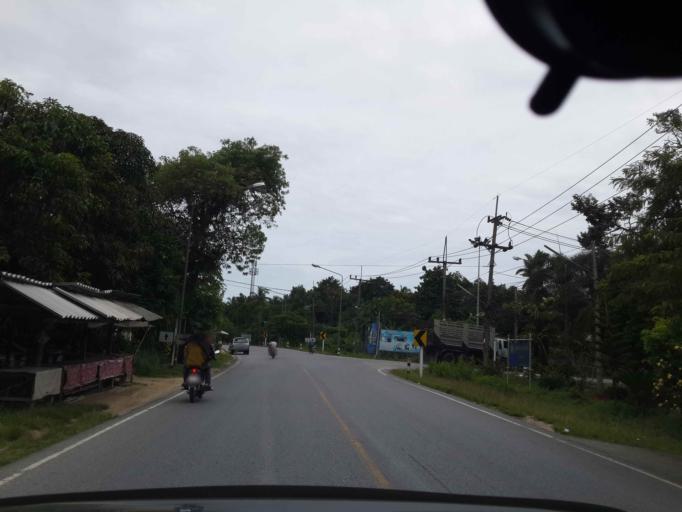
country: TH
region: Narathiwat
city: Yi-ngo
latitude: 6.3479
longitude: 101.6617
